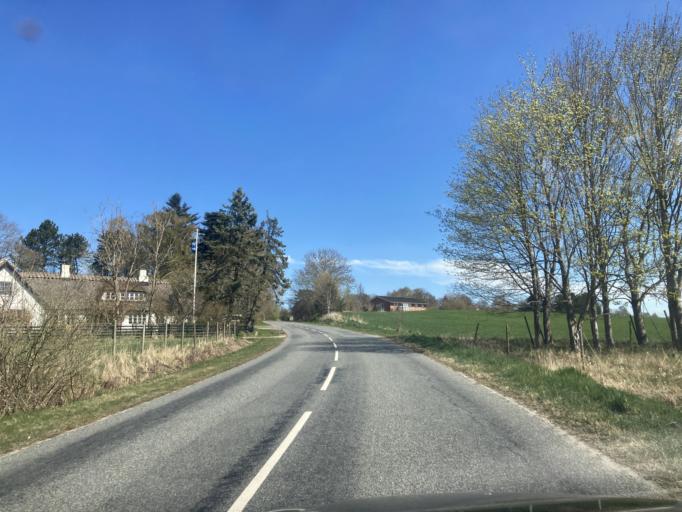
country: DK
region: Capital Region
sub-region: Gribskov Kommune
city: Helsinge
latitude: 56.0824
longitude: 12.1959
